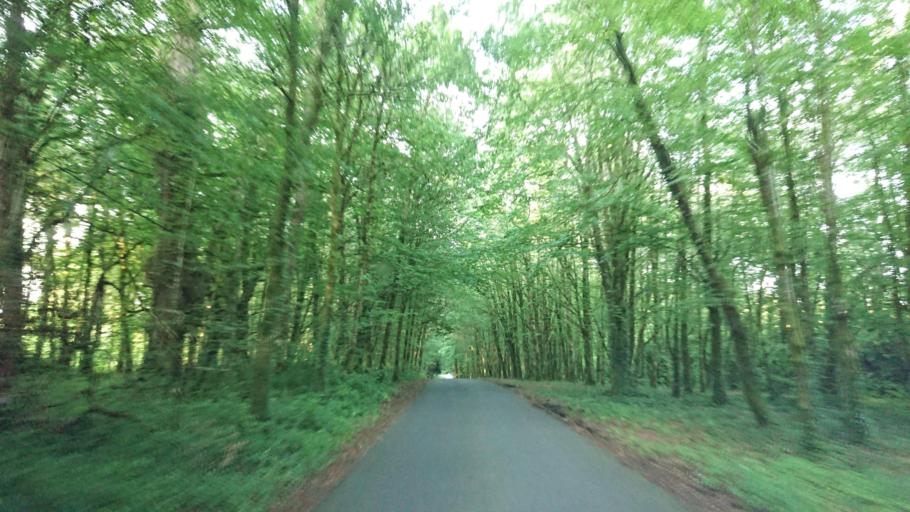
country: IE
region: Connaught
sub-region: Roscommon
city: Boyle
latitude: 53.9808
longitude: -8.2429
